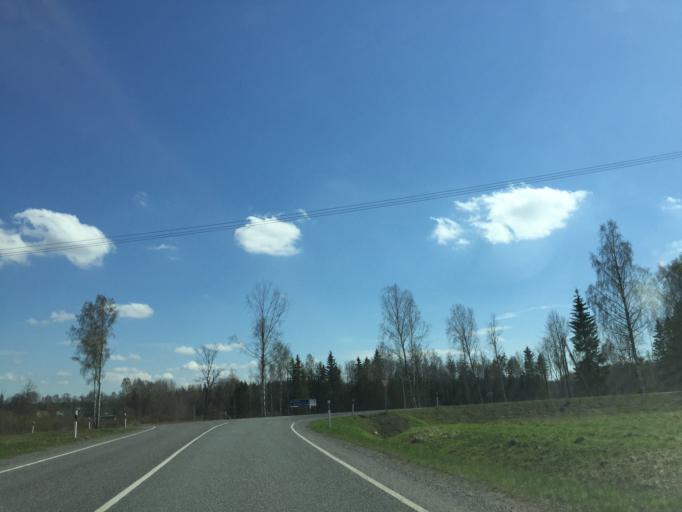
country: EE
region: Tartu
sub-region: Elva linn
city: Elva
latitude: 58.1469
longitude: 26.2303
